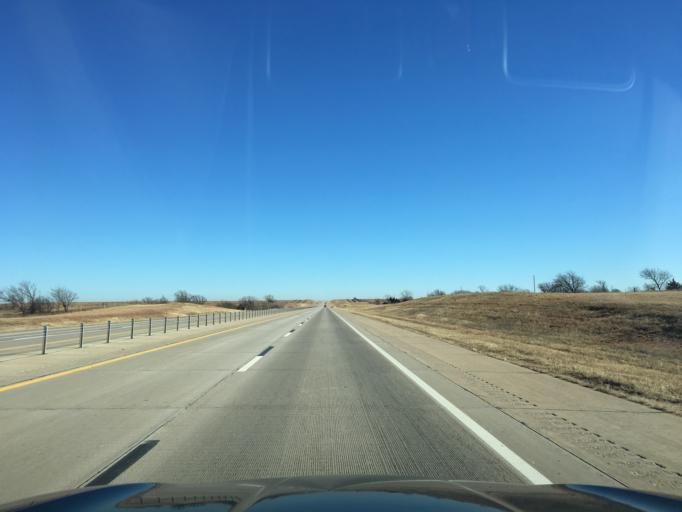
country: US
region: Oklahoma
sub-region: Noble County
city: Perry
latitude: 36.3920
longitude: -97.1706
